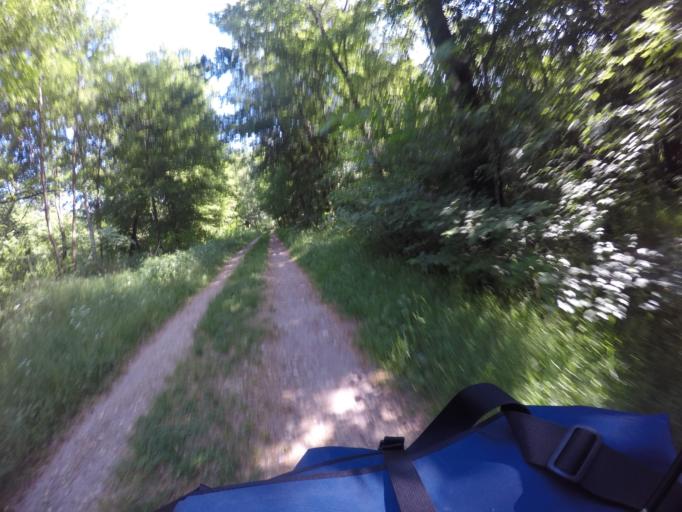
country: DE
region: Baden-Wuerttemberg
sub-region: Karlsruhe Region
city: Rheinstetten
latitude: 48.9404
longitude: 8.3123
